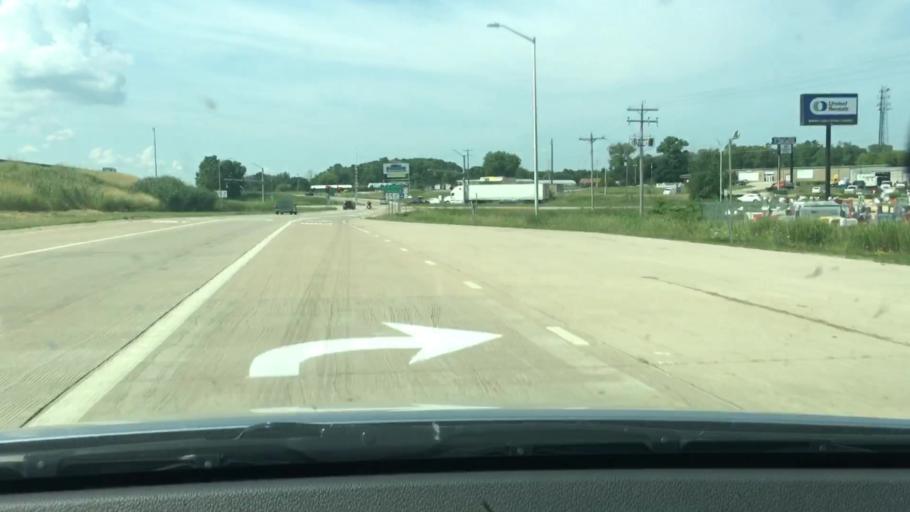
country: US
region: Wisconsin
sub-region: Winnebago County
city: Oshkosh
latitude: 44.0987
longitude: -88.5415
